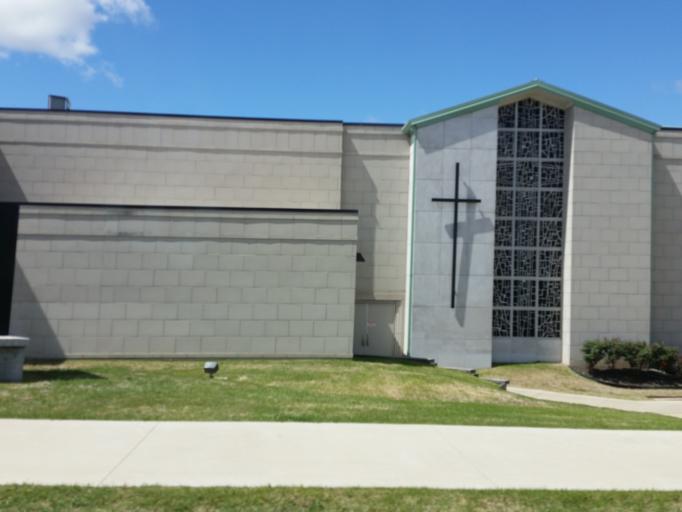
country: US
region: Arkansas
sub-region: Craighead County
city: Jonesboro
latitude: 35.8350
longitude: -90.7051
